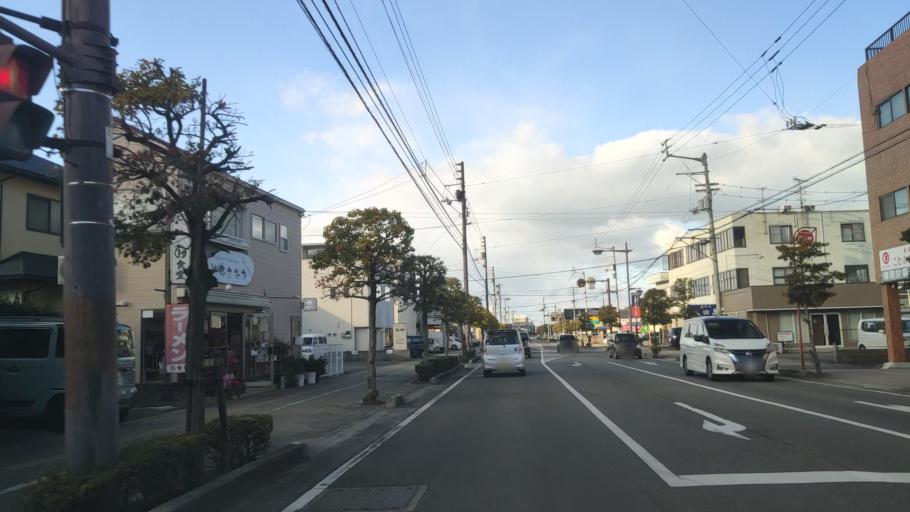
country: JP
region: Ehime
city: Saijo
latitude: 33.9196
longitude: 133.1851
